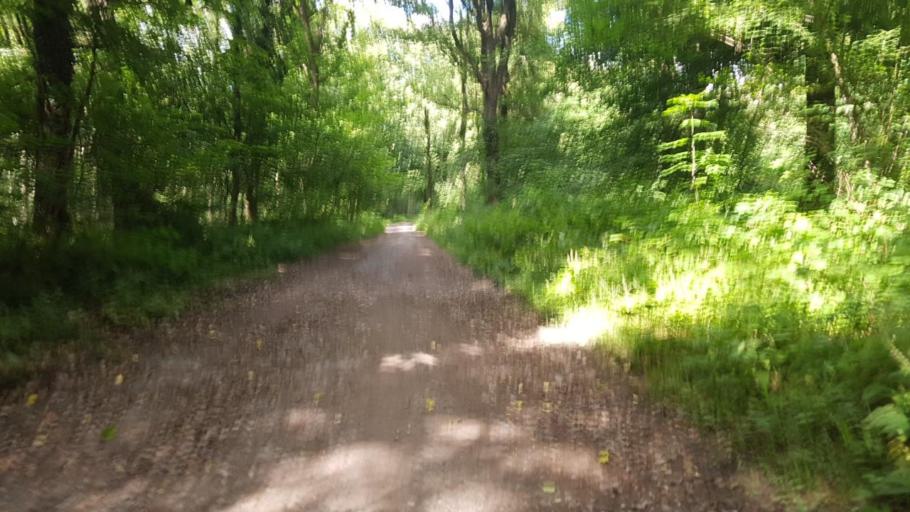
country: BE
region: Wallonia
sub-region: Province du Hainaut
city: Charleroi
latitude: 50.3577
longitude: 4.4459
